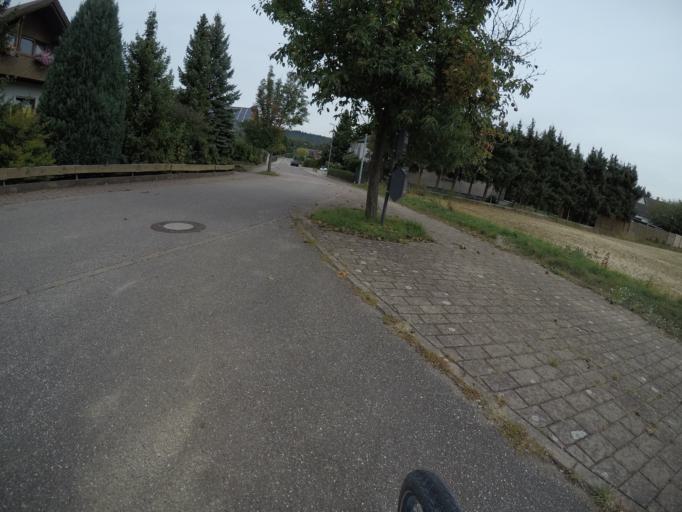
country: DE
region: Baden-Wuerttemberg
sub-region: Karlsruhe Region
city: Kurnbach
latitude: 49.0712
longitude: 8.8434
